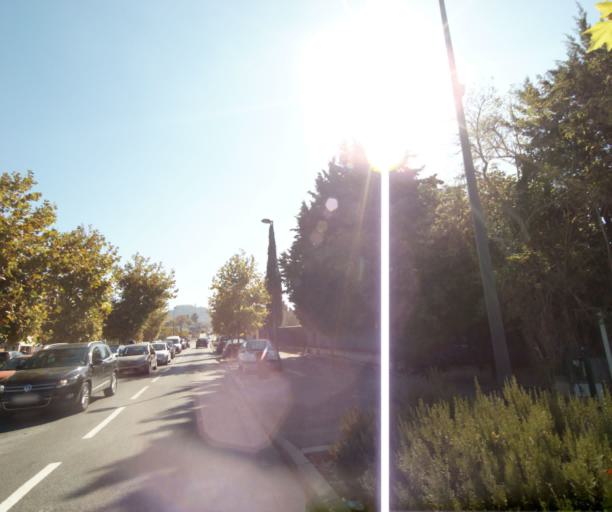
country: FR
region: Provence-Alpes-Cote d'Azur
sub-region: Departement des Bouches-du-Rhone
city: Plan-de-Cuques
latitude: 43.3428
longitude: 5.4692
